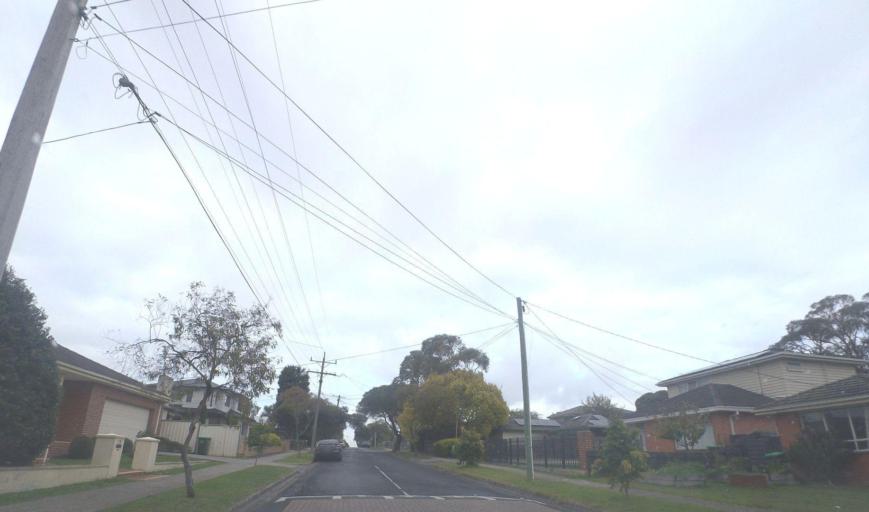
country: AU
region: Victoria
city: Mitcham
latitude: -37.8067
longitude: 145.1851
